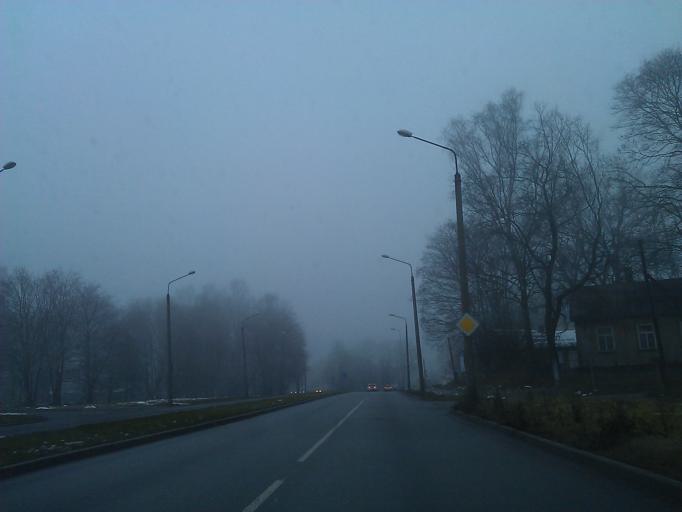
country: LV
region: Kekava
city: Balozi
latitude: 56.9123
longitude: 24.1242
